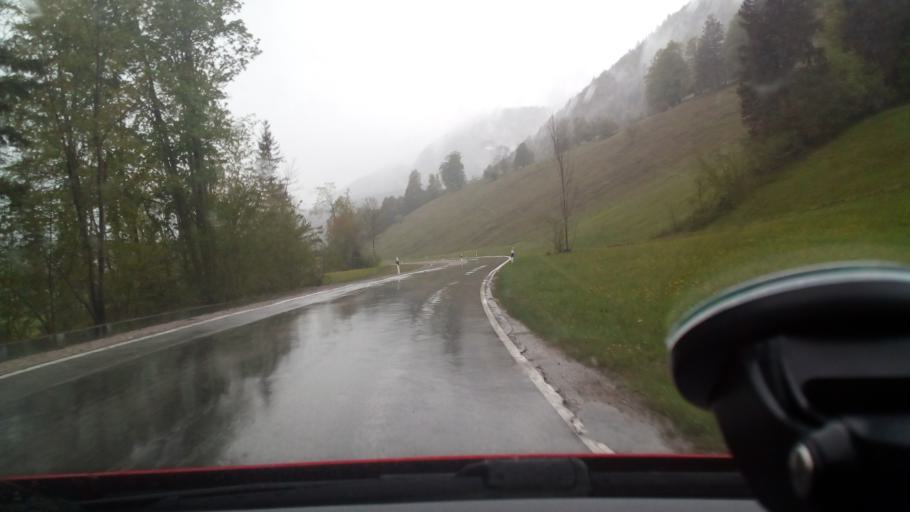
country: DE
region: Bavaria
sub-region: Upper Bavaria
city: Lenggries
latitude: 47.6301
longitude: 11.5347
